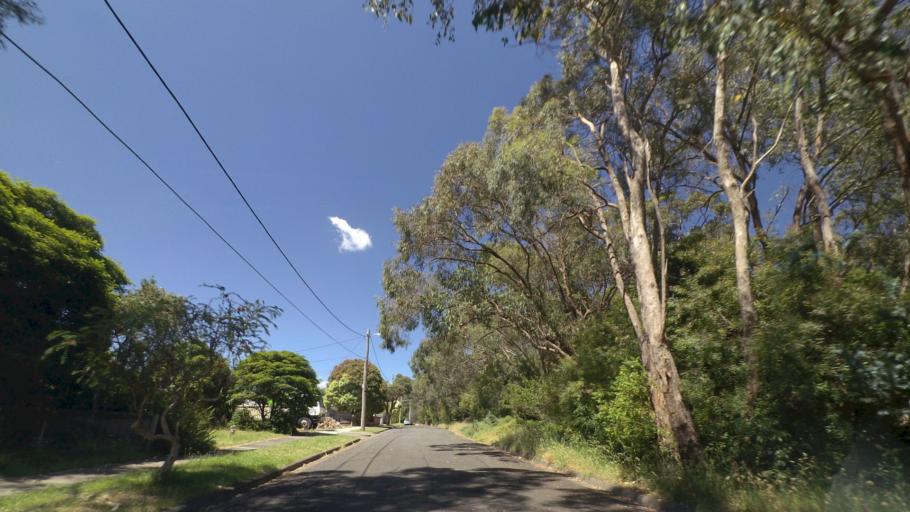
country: AU
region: Victoria
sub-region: Yarra Ranges
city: Kilsyth
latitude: -37.7983
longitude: 145.3150
